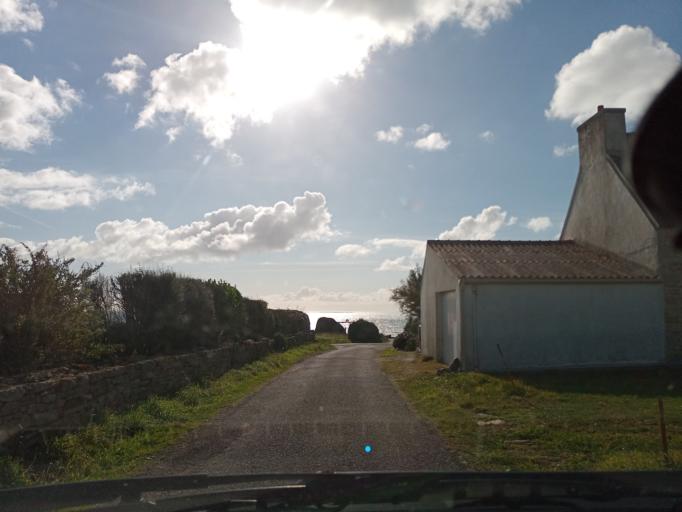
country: FR
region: Brittany
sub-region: Departement du Finistere
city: Plozevet
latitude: 47.9745
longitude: -4.4431
